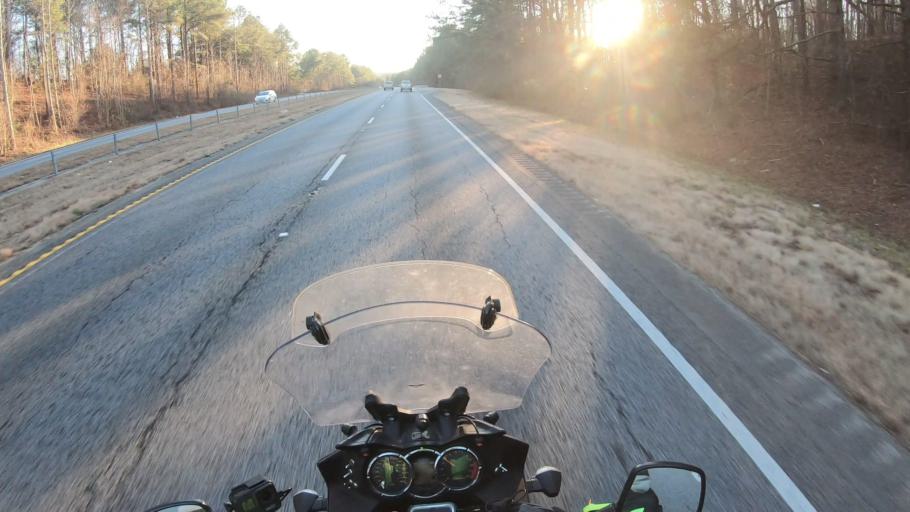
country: US
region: Georgia
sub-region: Dawson County
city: Dawsonville
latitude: 34.3920
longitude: -84.0190
